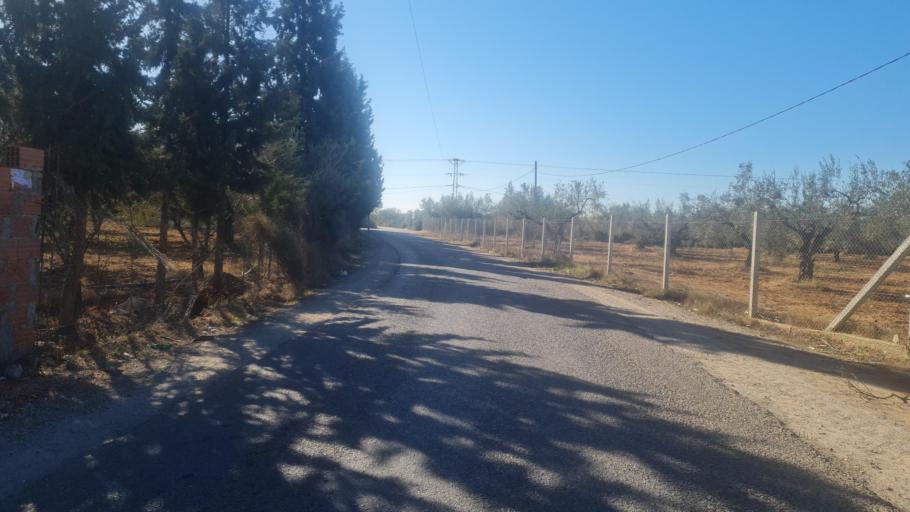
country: TN
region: Susah
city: Sidi Bou Ali
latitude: 35.9100
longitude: 10.3816
